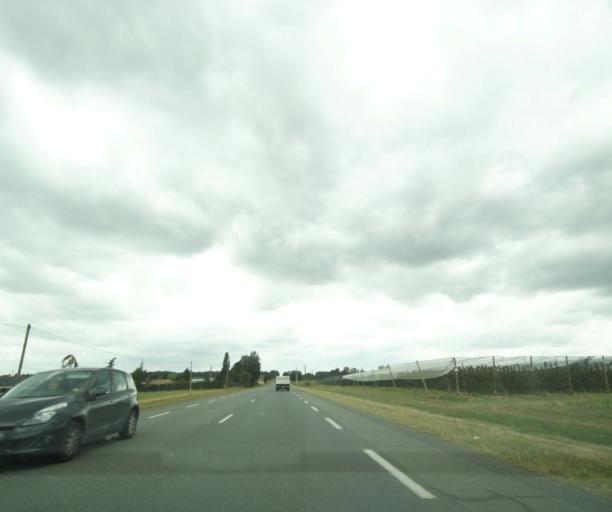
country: FR
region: Pays de la Loire
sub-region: Departement de Maine-et-Loire
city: Durtal
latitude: 47.6479
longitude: -0.2683
